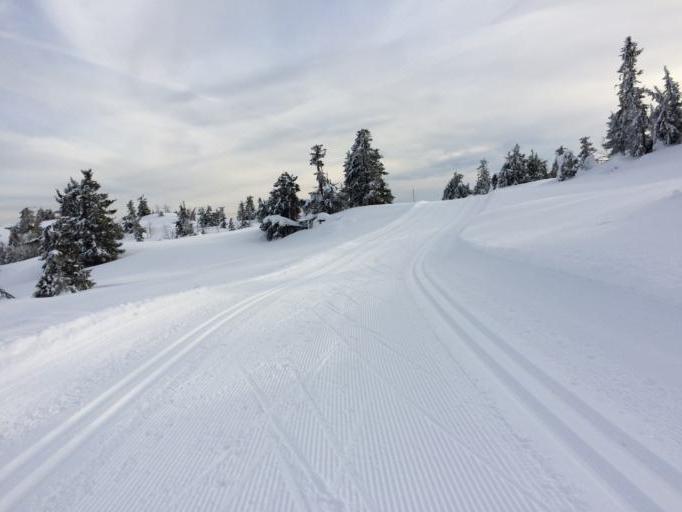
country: NO
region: Oppland
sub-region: Gausdal
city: Segalstad bru
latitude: 61.3231
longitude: 10.0409
